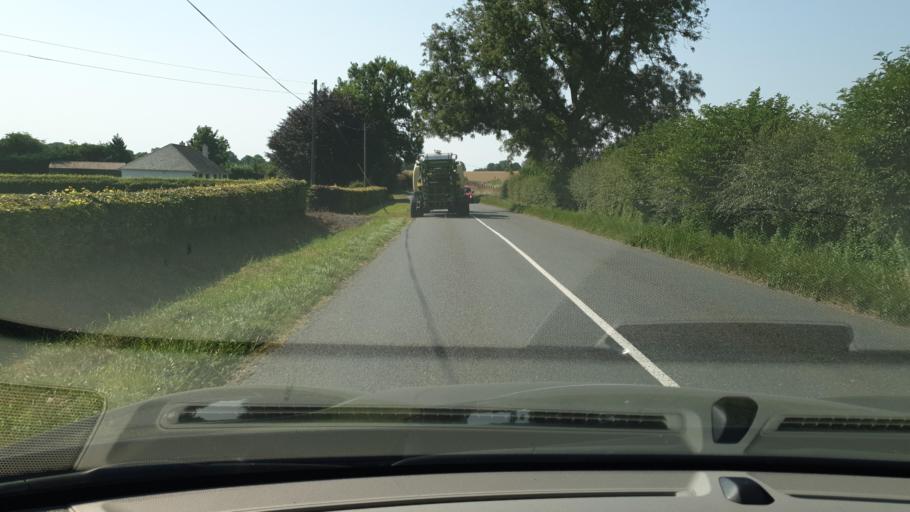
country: IE
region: Leinster
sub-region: An Mhi
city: Athboy
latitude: 53.5925
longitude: -6.8621
